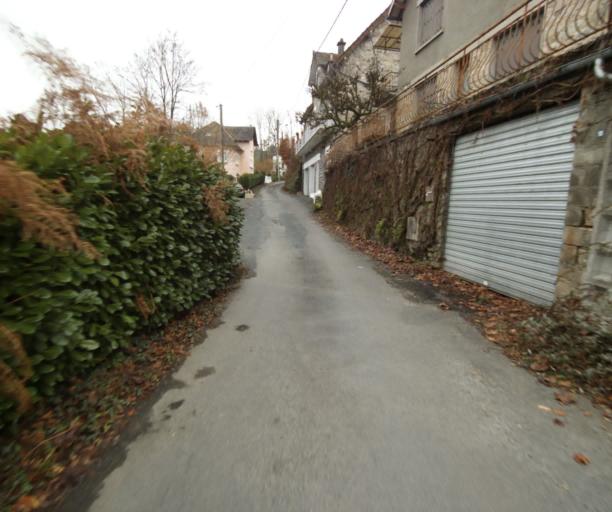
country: FR
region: Limousin
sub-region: Departement de la Correze
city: Tulle
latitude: 45.2624
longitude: 1.7438
